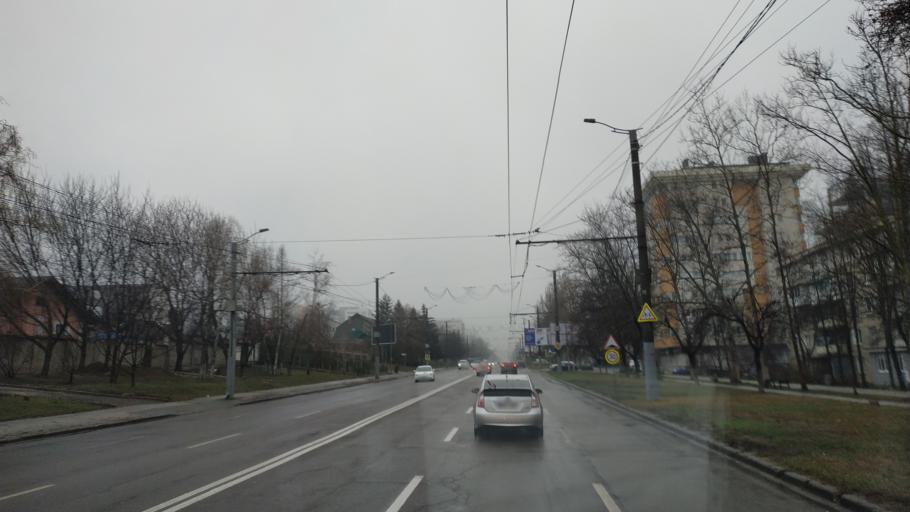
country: MD
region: Chisinau
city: Vatra
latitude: 47.0303
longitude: 28.7865
